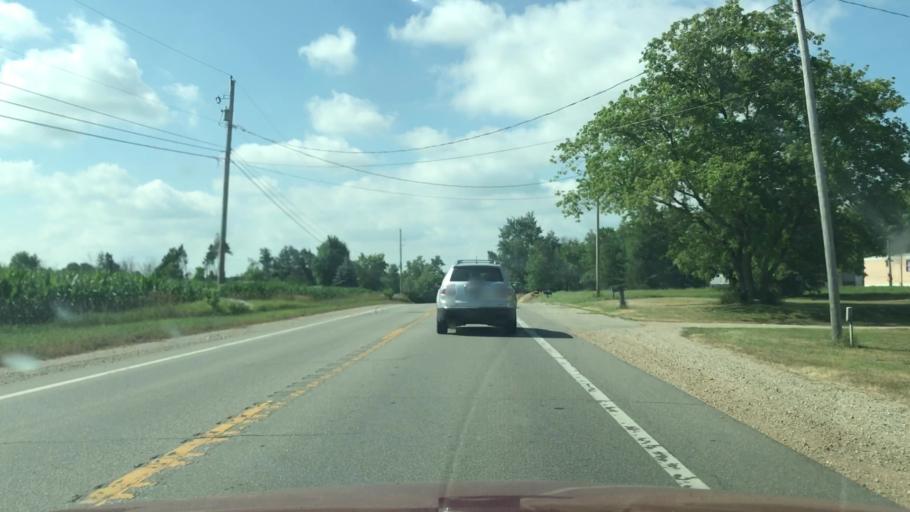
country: US
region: Michigan
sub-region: Kent County
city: Kent City
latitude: 43.3031
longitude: -85.8106
